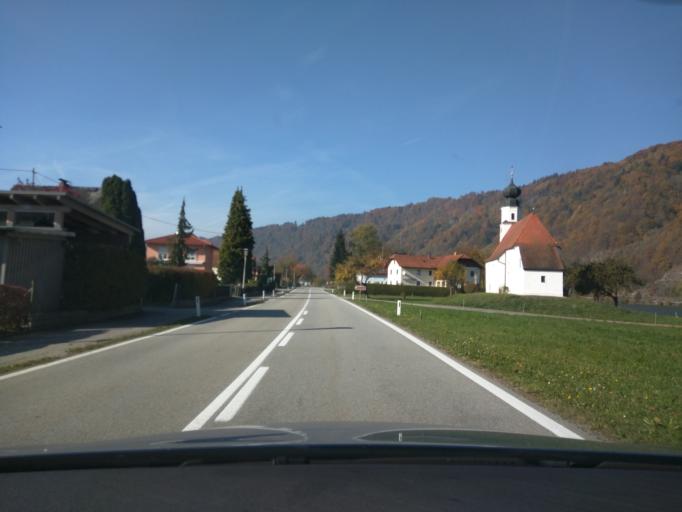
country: DE
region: Bavaria
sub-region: Lower Bavaria
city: Obernzell
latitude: 48.5633
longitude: 13.6078
